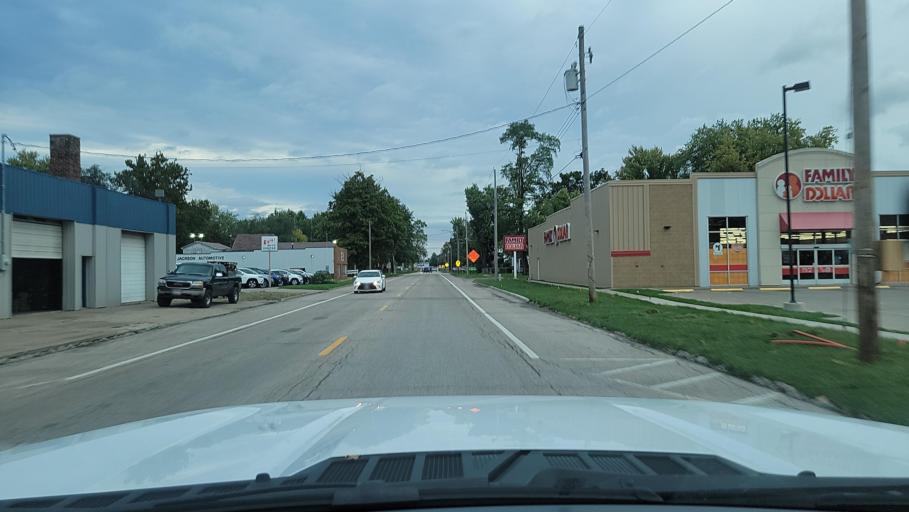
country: US
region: Illinois
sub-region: Schuyler County
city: Rushville
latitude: 40.1239
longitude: -90.5636
